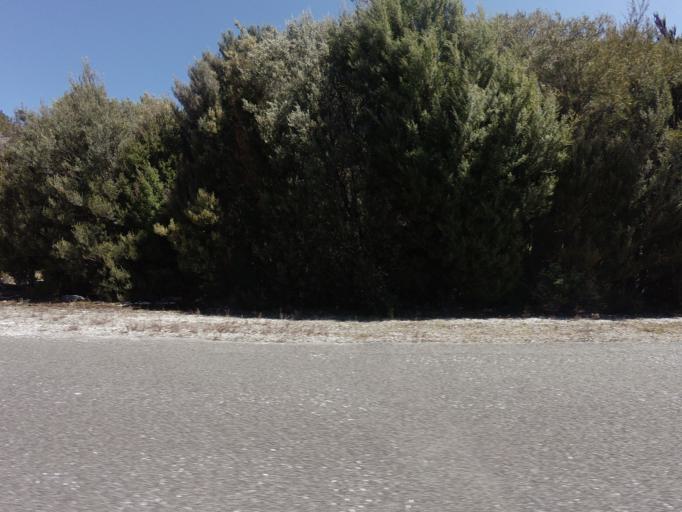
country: AU
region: Tasmania
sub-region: West Coast
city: Queenstown
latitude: -42.7569
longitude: 146.0026
